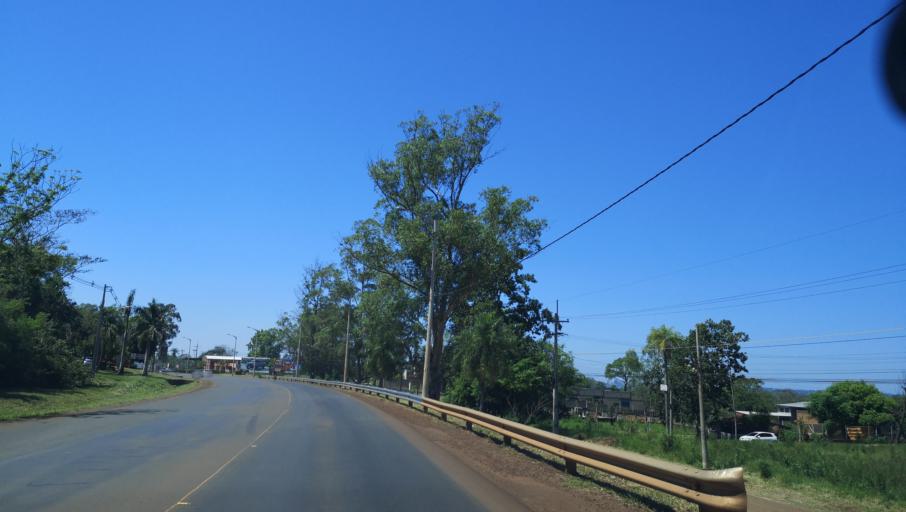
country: PY
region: Itapua
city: San Juan del Parana
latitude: -27.2917
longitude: -55.9342
